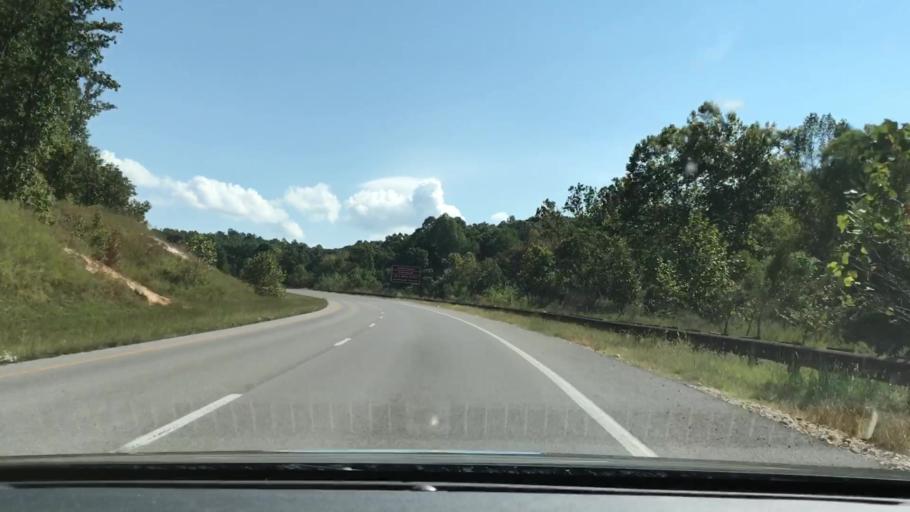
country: US
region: Kentucky
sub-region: Trigg County
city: Cadiz
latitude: 36.7776
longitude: -88.0874
